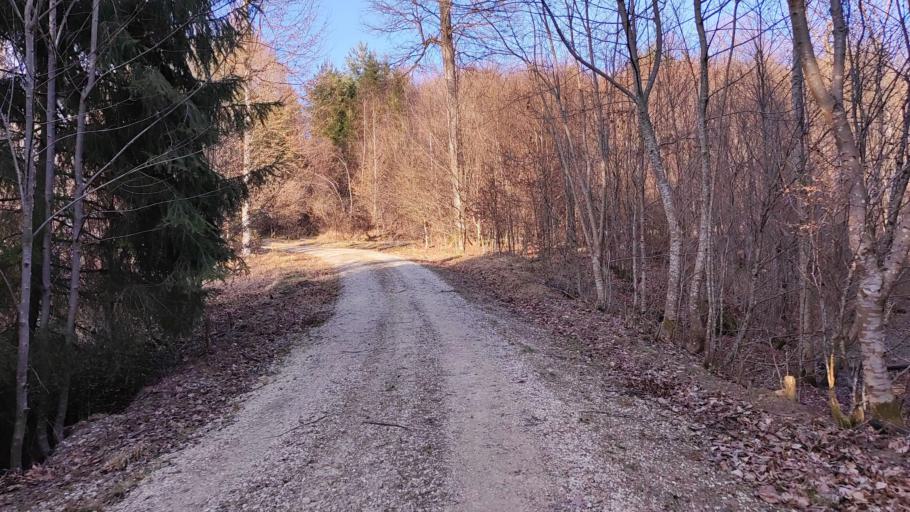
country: DE
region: Bavaria
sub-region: Swabia
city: Zusmarshausen
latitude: 48.4292
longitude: 10.6201
